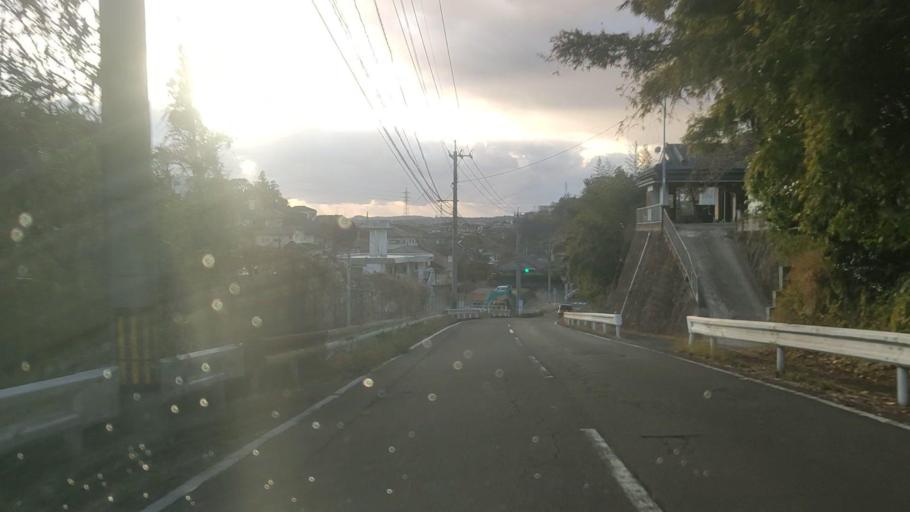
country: JP
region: Kagoshima
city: Kagoshima-shi
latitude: 31.6273
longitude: 130.5502
